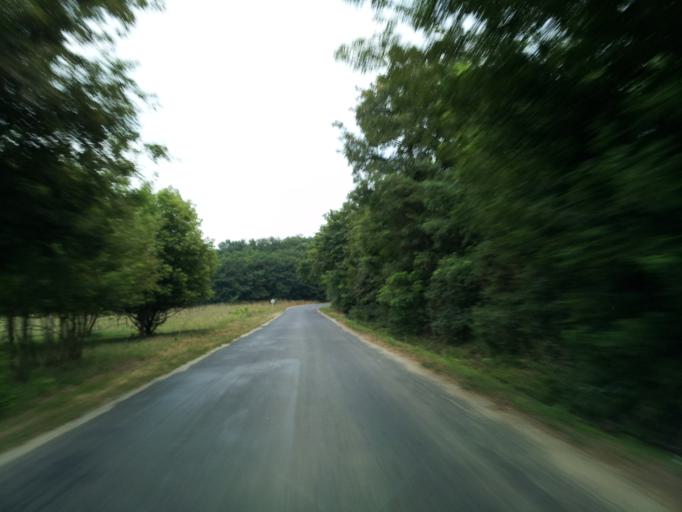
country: HU
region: Vas
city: Sarvar
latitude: 47.2063
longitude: 16.9426
